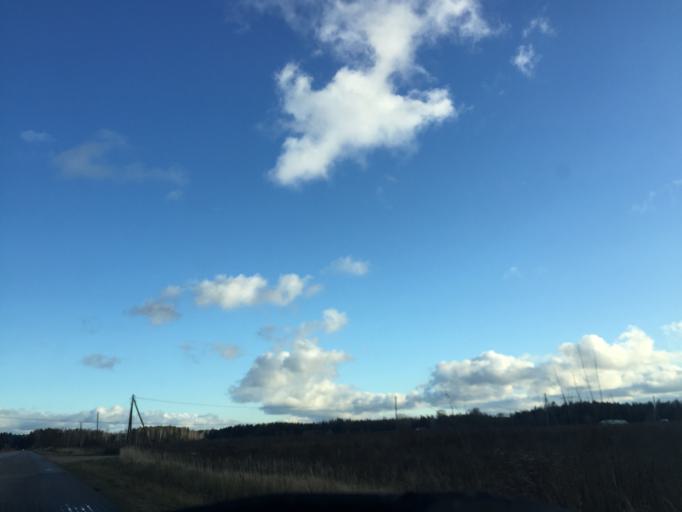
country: LV
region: Incukalns
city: Incukalns
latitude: 57.0927
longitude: 24.7148
